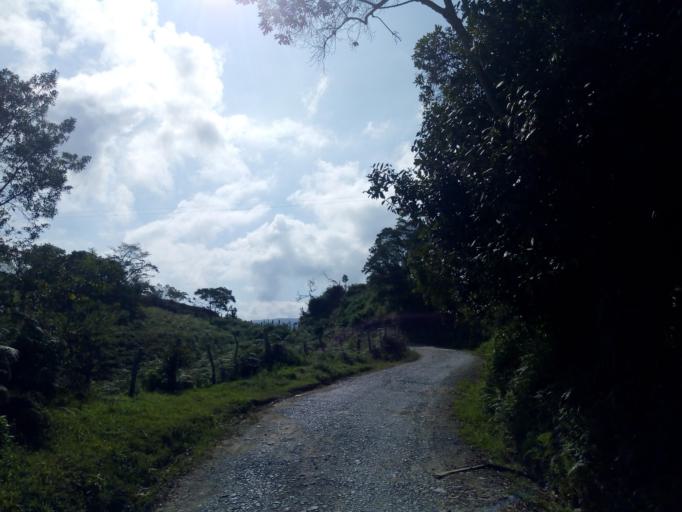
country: CO
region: Boyaca
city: Moniquira
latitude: 5.8834
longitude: -73.5101
